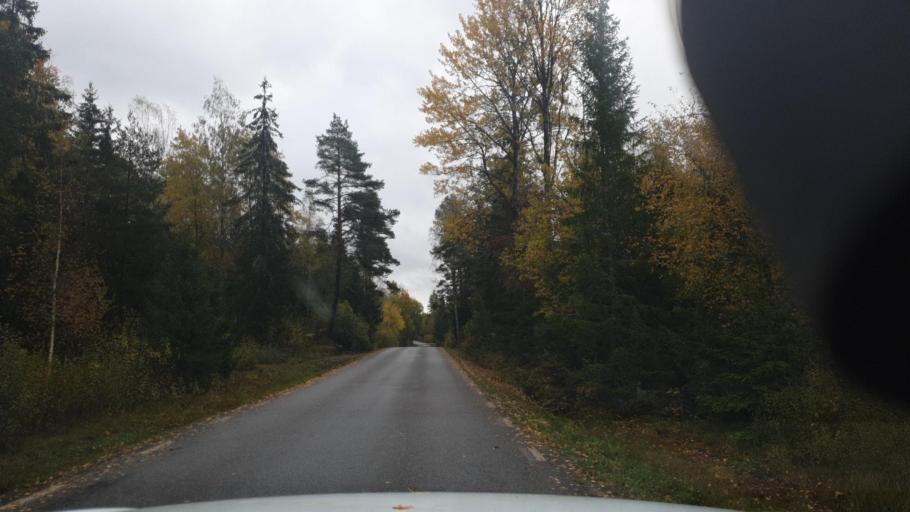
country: SE
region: Vaermland
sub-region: Karlstads Kommun
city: Valberg
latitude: 59.4179
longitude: 13.1191
